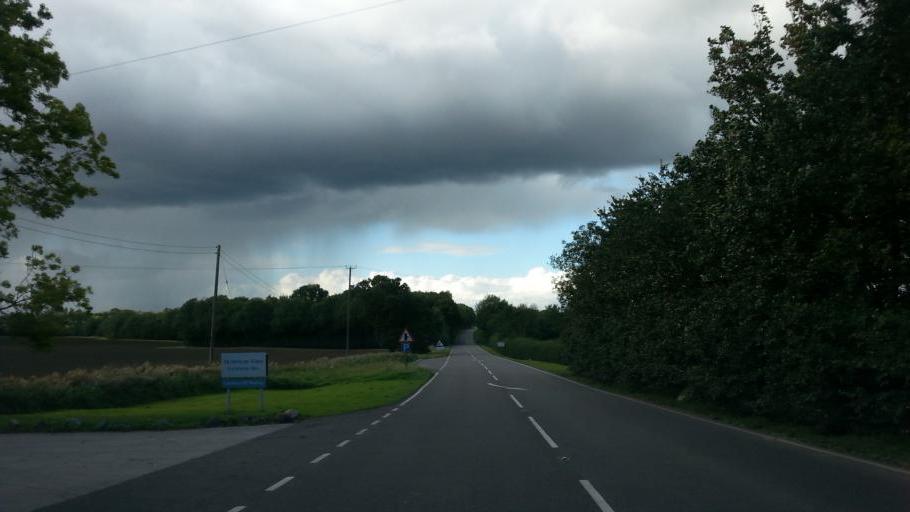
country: GB
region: England
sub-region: Cambridgeshire
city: Papworth Everard
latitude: 52.2815
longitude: -0.1413
